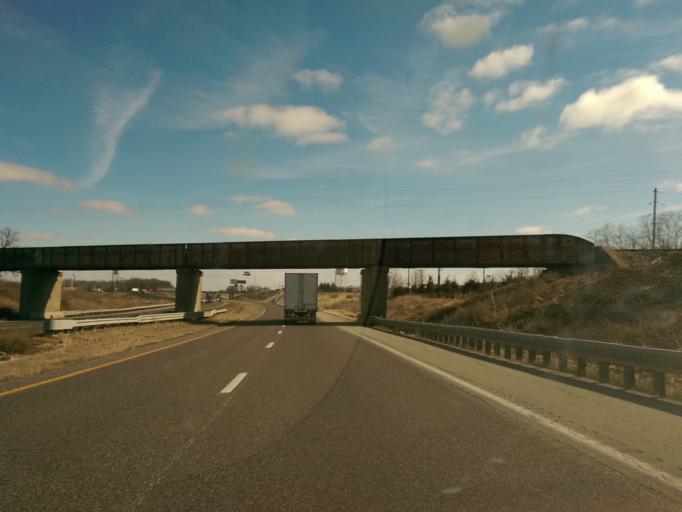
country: US
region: Missouri
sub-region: Callaway County
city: Fulton
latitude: 38.9447
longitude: -91.9483
